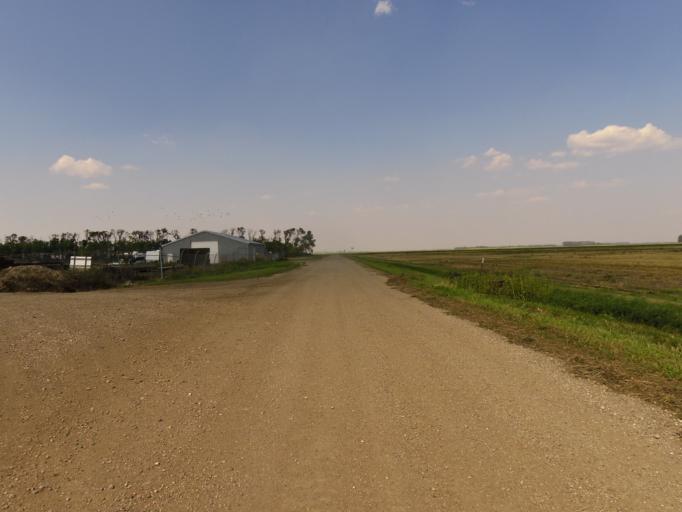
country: US
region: North Dakota
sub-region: Walsh County
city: Grafton
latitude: 48.4315
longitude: -97.3972
